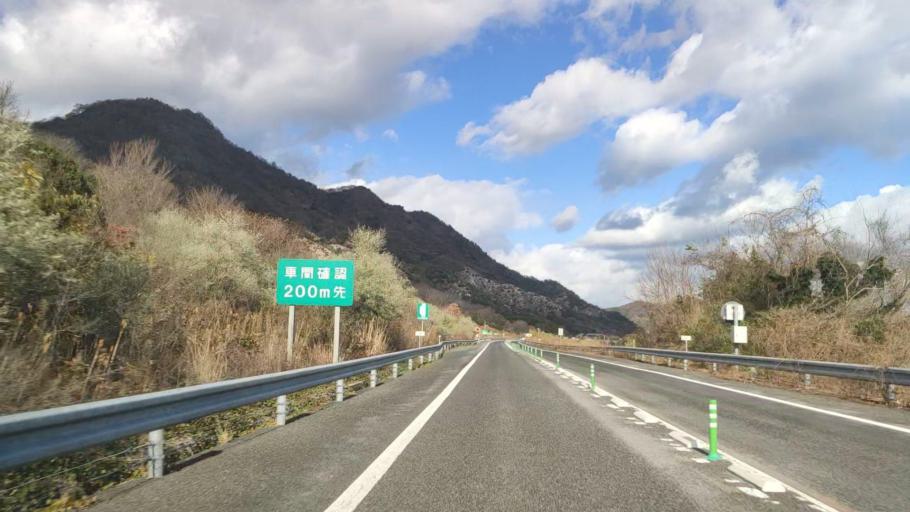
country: JP
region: Hiroshima
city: Innoshima
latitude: 34.2657
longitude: 133.0958
